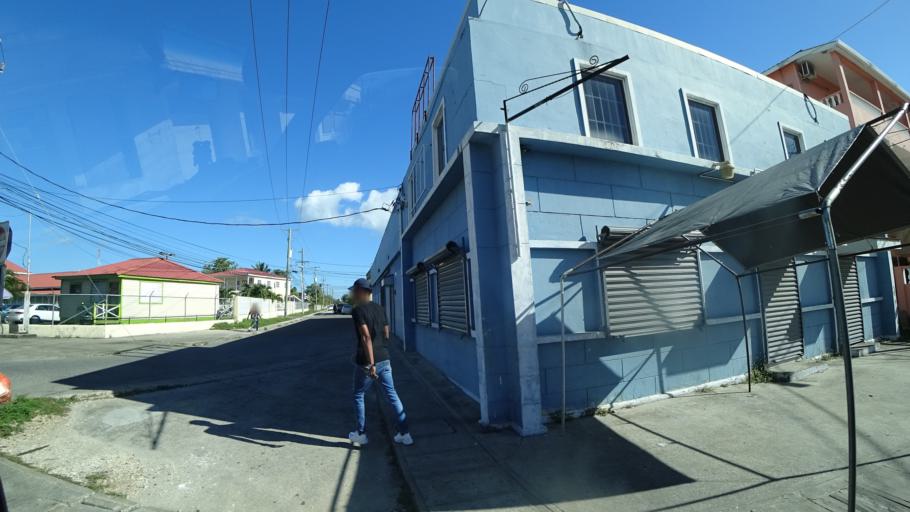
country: BZ
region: Belize
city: Belize City
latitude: 17.5022
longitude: -88.1919
